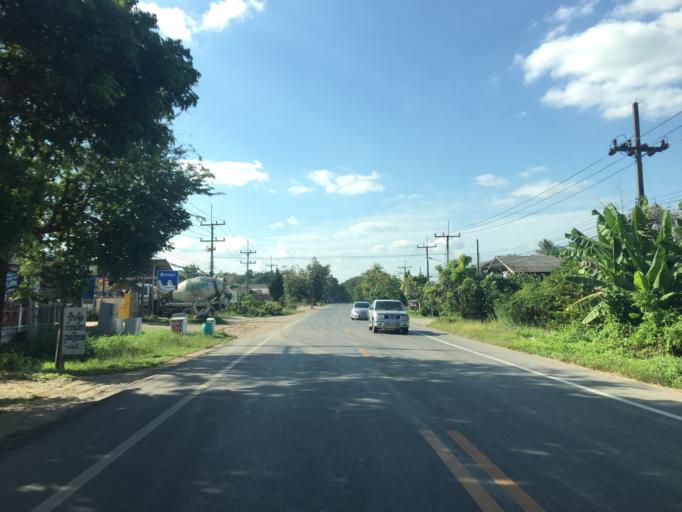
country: TH
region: Phayao
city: Chun
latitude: 19.3453
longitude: 100.1173
